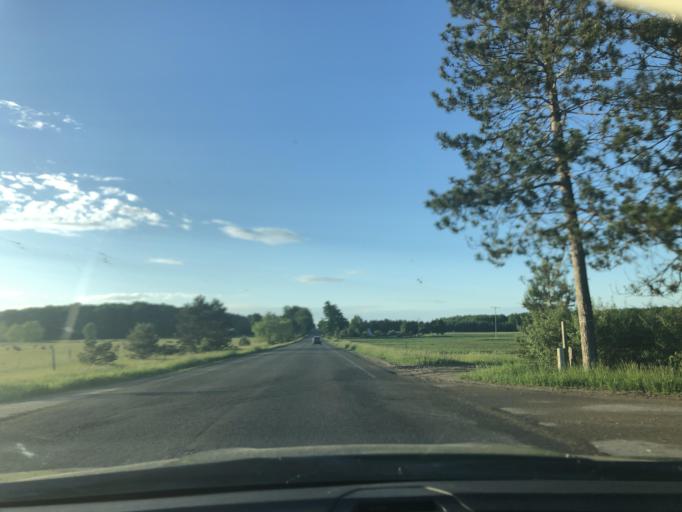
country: US
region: Michigan
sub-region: Missaukee County
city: Lake City
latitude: 44.3946
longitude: -85.0757
